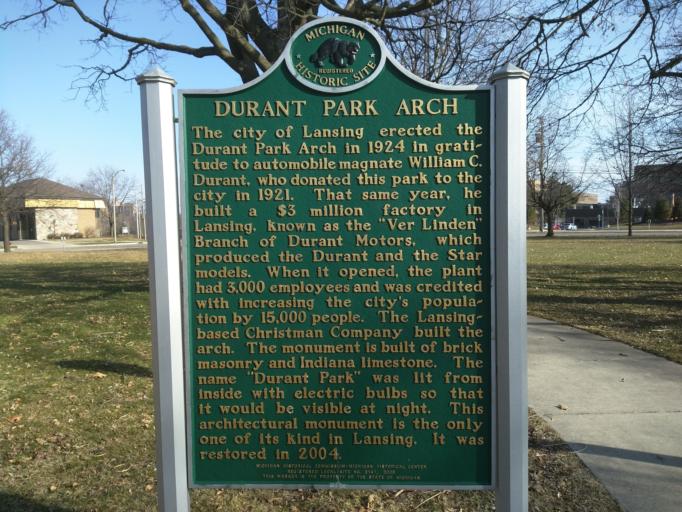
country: US
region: Michigan
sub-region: Ingham County
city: Lansing
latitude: 42.7415
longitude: -84.5529
